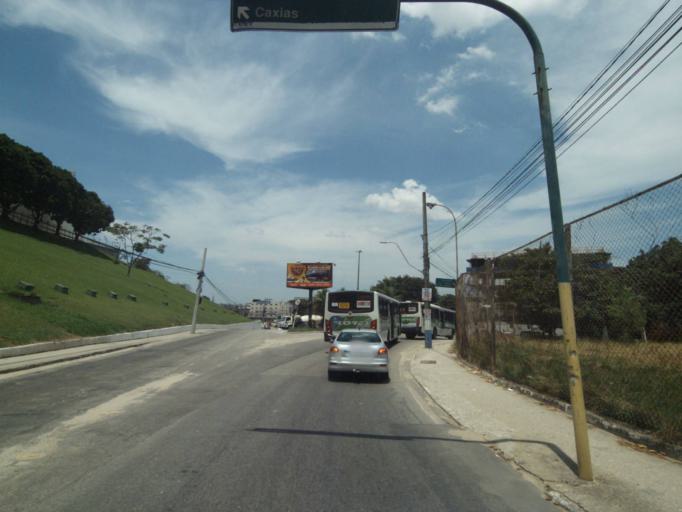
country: BR
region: Rio de Janeiro
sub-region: Sao Joao De Meriti
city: Sao Joao de Meriti
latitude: -22.7988
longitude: -43.3532
